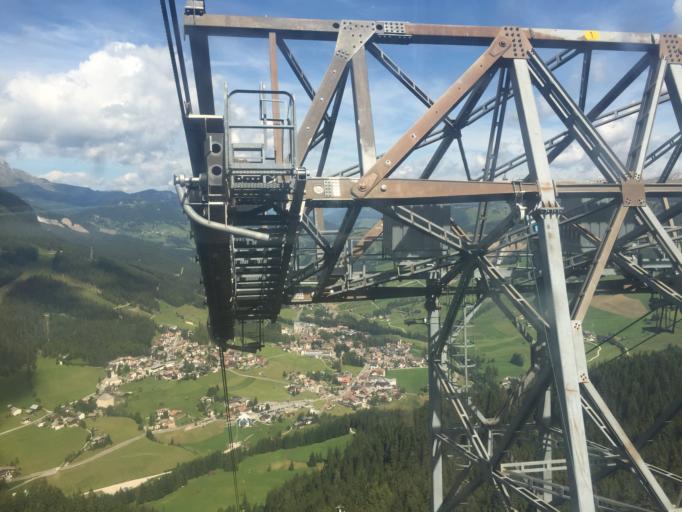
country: IT
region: Trentino-Alto Adige
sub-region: Bolzano
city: Corvara in Badia
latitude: 46.5703
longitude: 11.9045
